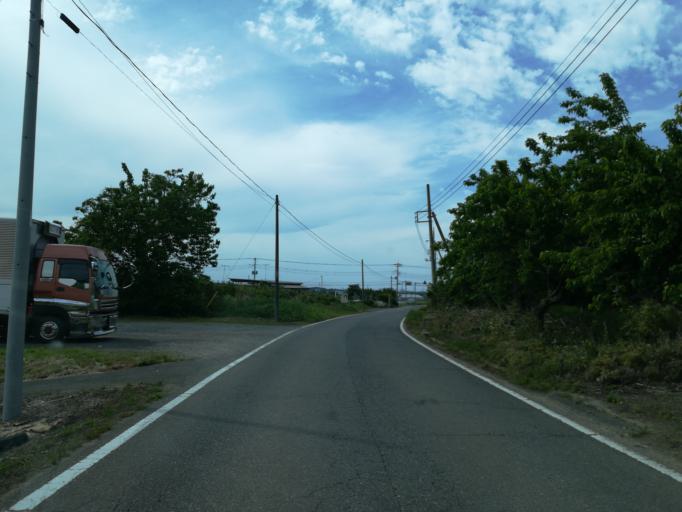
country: JP
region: Ibaraki
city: Tsukuba
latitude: 36.1892
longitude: 140.0901
